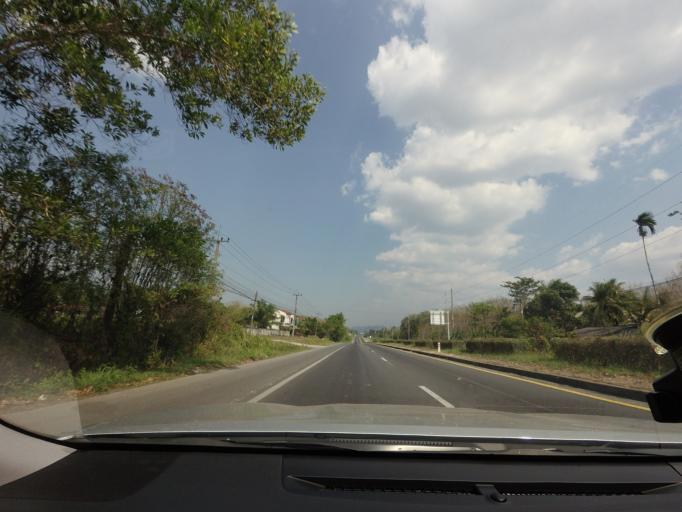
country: TH
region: Phangnga
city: Thap Put
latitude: 8.5087
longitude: 98.6588
